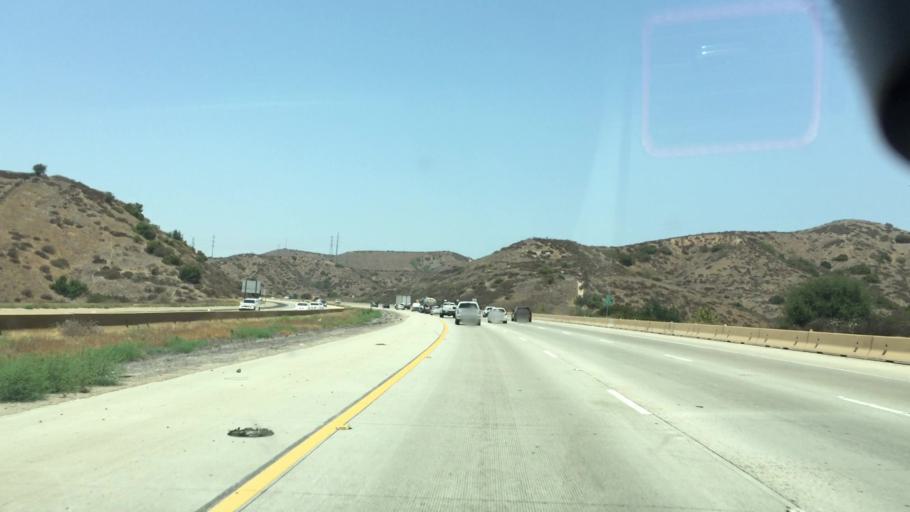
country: US
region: California
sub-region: San Diego County
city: Santee
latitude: 32.8490
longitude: -117.0302
